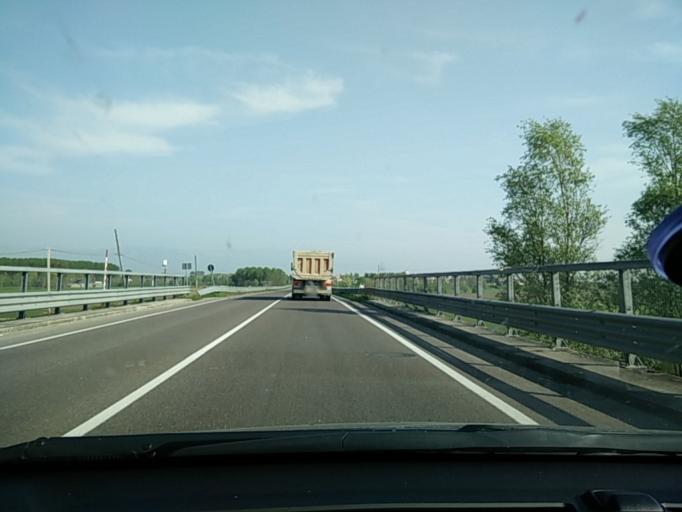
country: IT
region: Veneto
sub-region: Provincia di Treviso
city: Portobuffole
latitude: 45.8447
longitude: 12.5372
